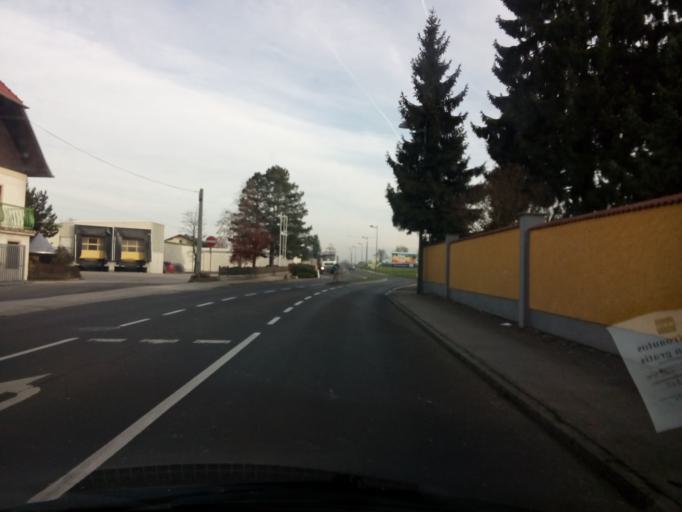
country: AT
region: Upper Austria
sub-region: Wels-Land
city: Sattledt
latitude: 48.0729
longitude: 14.0614
